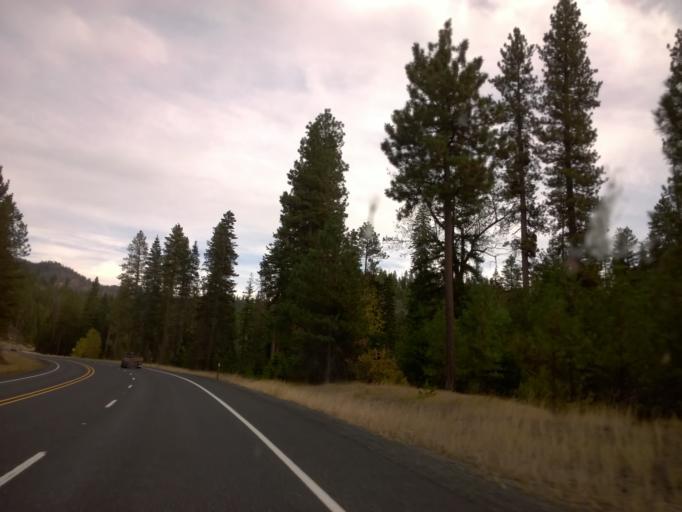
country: US
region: Washington
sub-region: Chelan County
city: Cashmere
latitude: 47.3700
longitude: -120.5836
